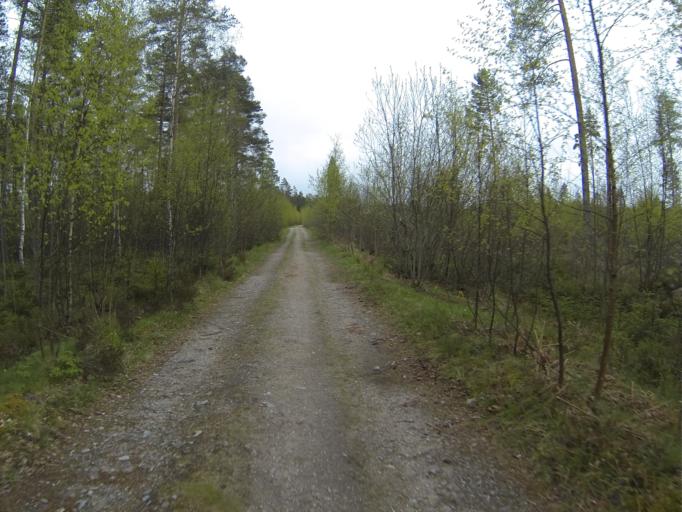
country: FI
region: Varsinais-Suomi
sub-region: Salo
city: Salo
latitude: 60.3951
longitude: 23.1973
